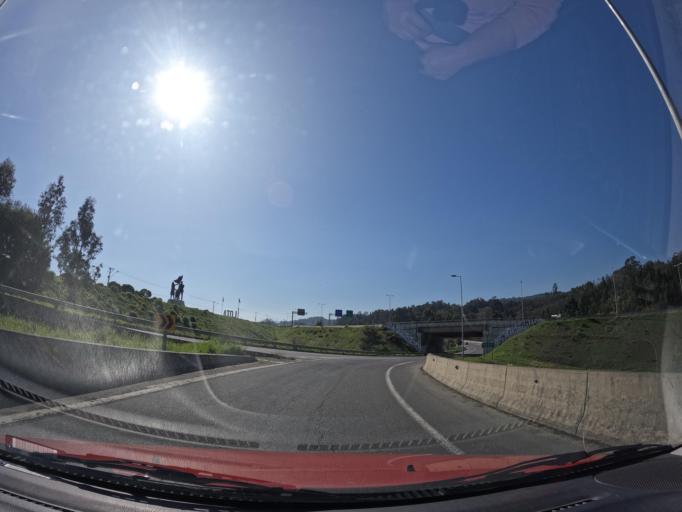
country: CL
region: Biobio
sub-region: Provincia de Concepcion
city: Lota
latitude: -37.0715
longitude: -73.1454
